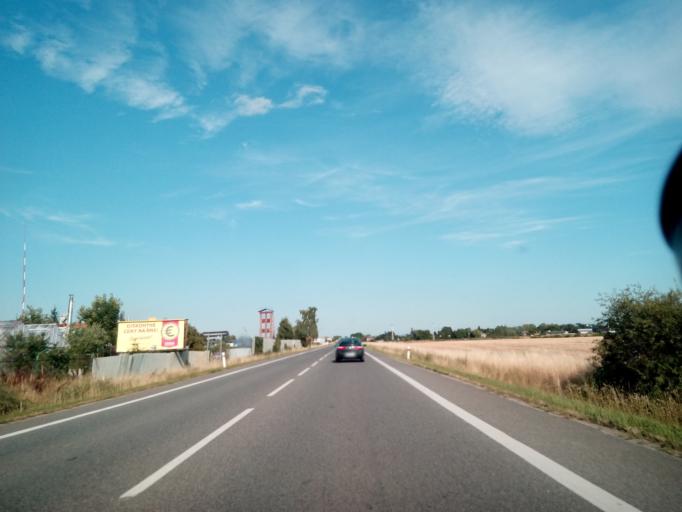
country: SK
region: Kosicky
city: Moldava nad Bodvou
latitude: 48.6080
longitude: 20.9880
